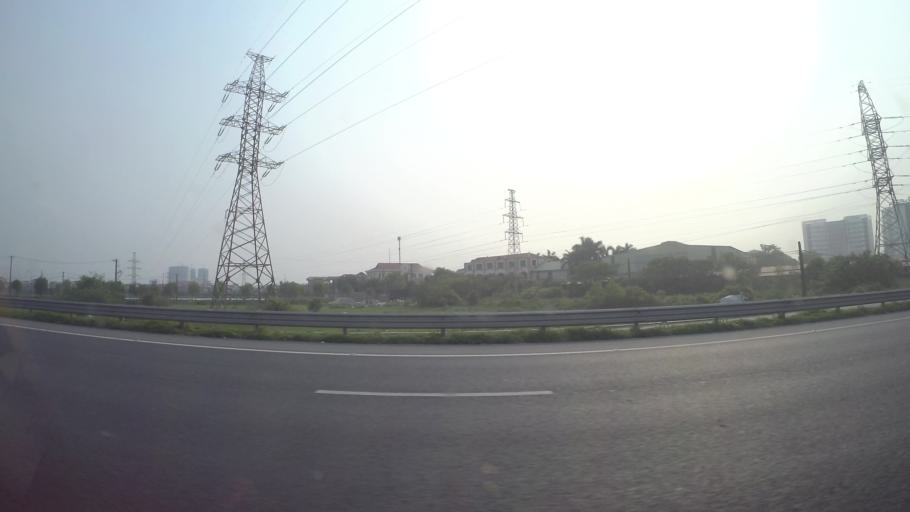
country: VN
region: Ha Noi
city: Van Dien
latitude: 20.9474
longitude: 105.8568
